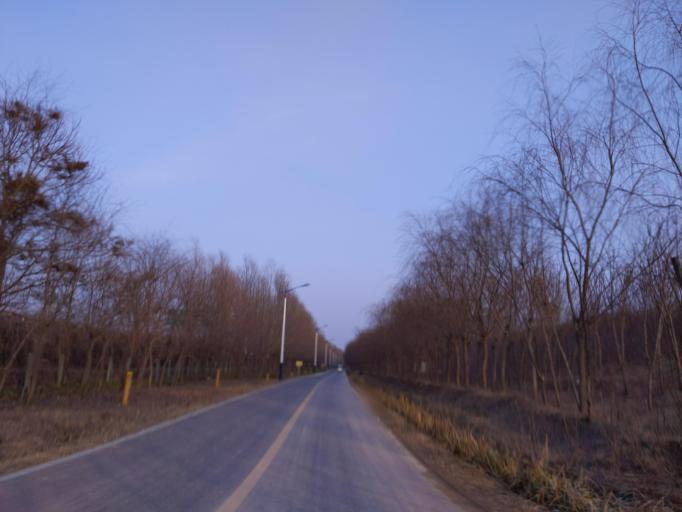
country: CN
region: Henan Sheng
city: Puyang
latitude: 35.8212
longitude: 115.0127
